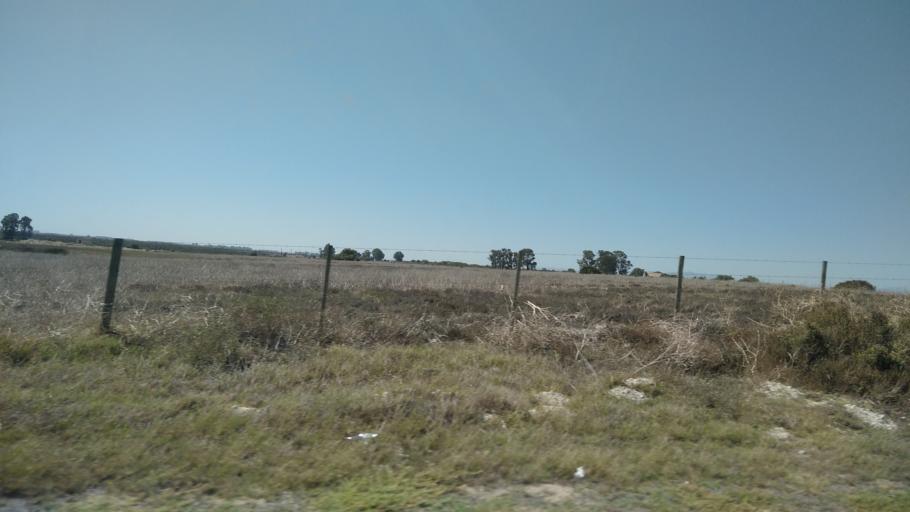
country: ZA
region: Western Cape
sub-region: West Coast District Municipality
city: Vredenburg
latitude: -32.9963
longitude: 18.1844
